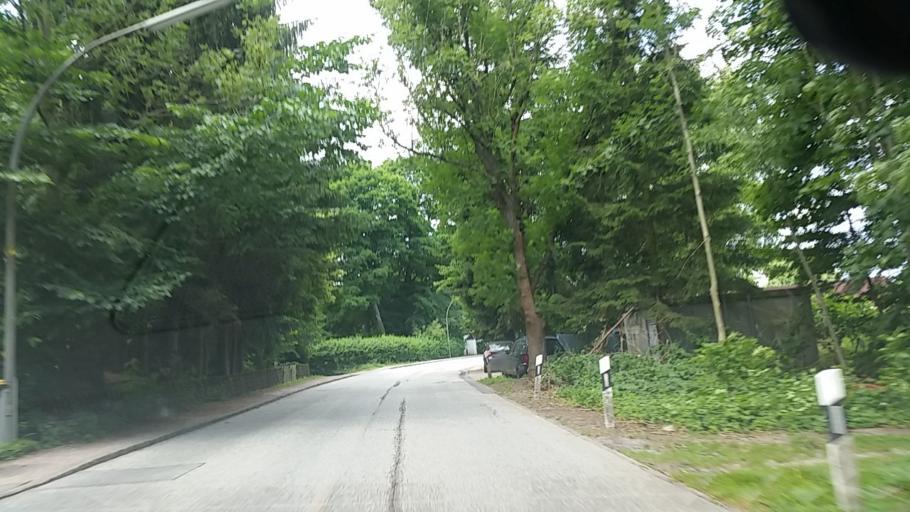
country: DE
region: Hamburg
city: Wandsbek
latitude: 53.5243
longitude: 10.1112
